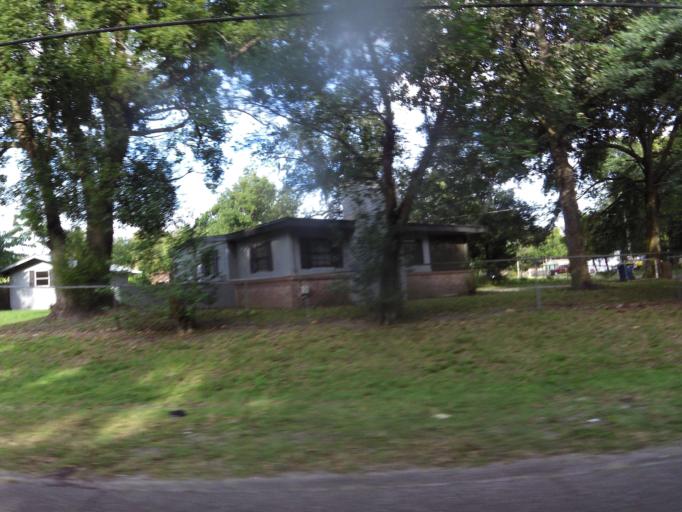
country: US
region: Florida
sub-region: Duval County
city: Jacksonville
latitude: 30.4261
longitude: -81.6725
